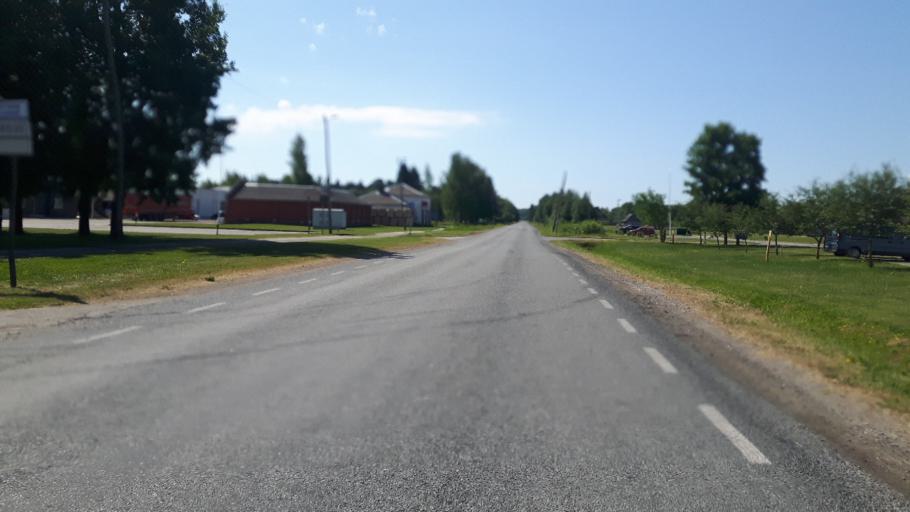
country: EE
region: Paernumaa
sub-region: Vaendra vald (alev)
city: Vandra
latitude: 58.6456
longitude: 25.0287
